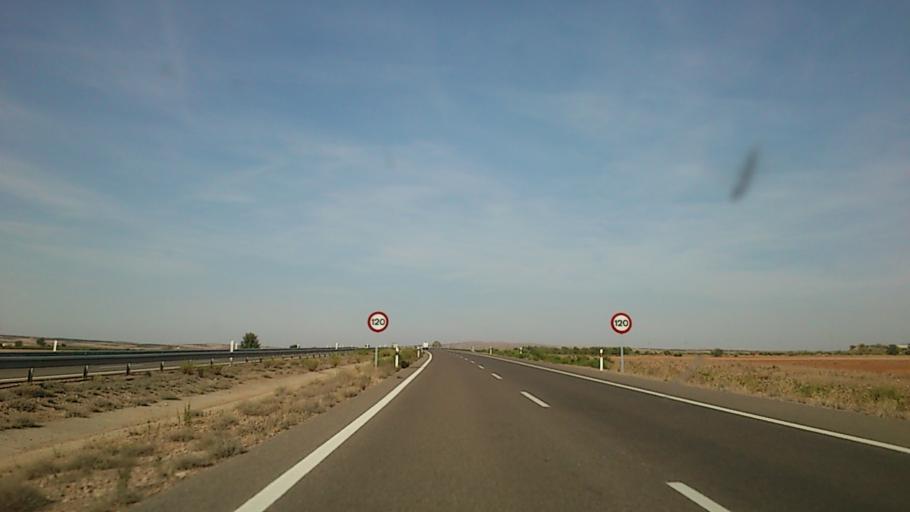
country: ES
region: Aragon
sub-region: Provincia de Zaragoza
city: Longares
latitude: 41.3800
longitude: -1.1928
